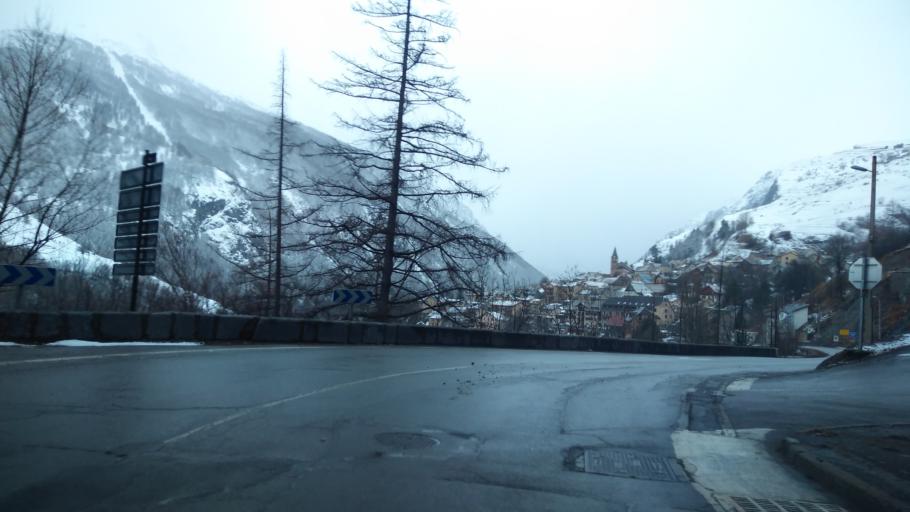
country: FR
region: Rhone-Alpes
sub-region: Departement de la Savoie
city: Valloire
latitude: 45.0483
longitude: 6.3140
